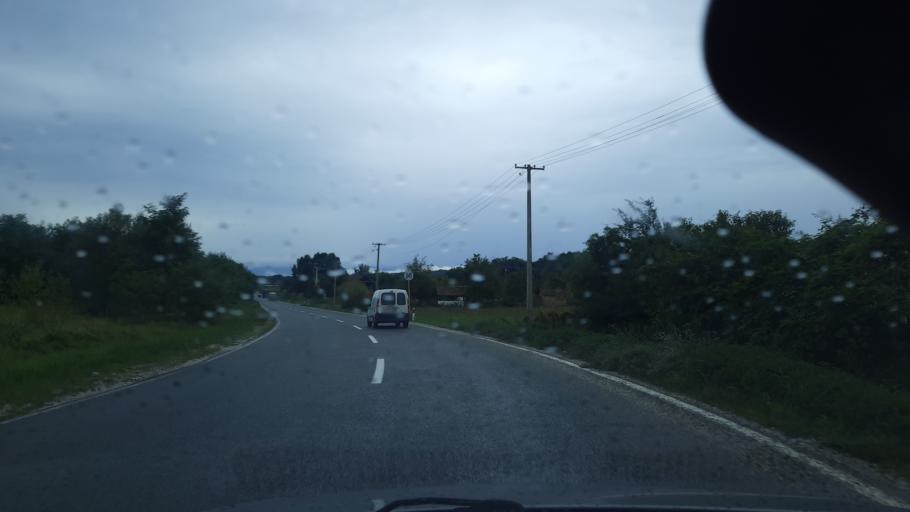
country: RS
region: Central Serbia
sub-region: Raski Okrug
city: Kraljevo
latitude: 43.8035
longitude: 20.7867
